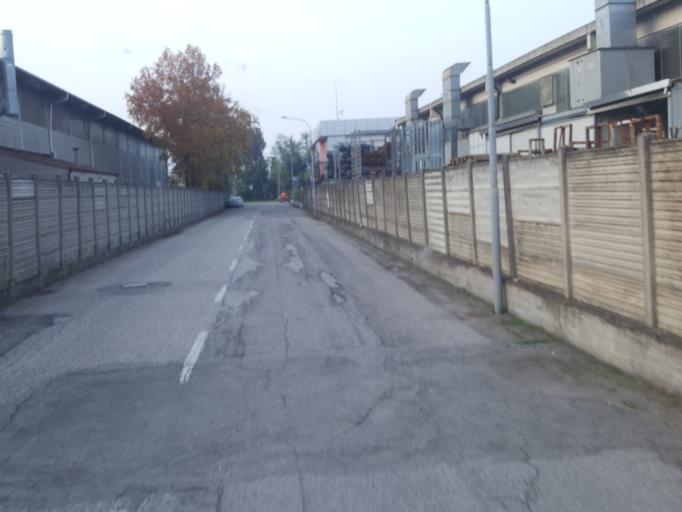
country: IT
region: Veneto
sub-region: Provincia di Verona
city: Zevio
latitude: 45.3707
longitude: 11.0941
